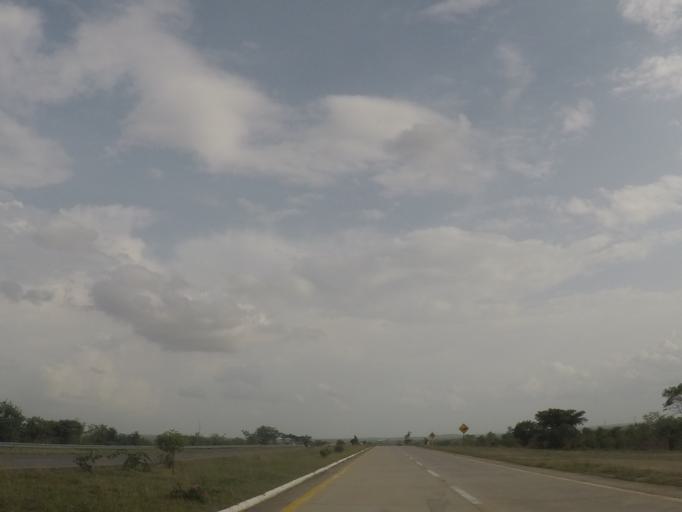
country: MM
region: Mandalay
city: Meiktila
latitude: 20.6174
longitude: 95.8156
